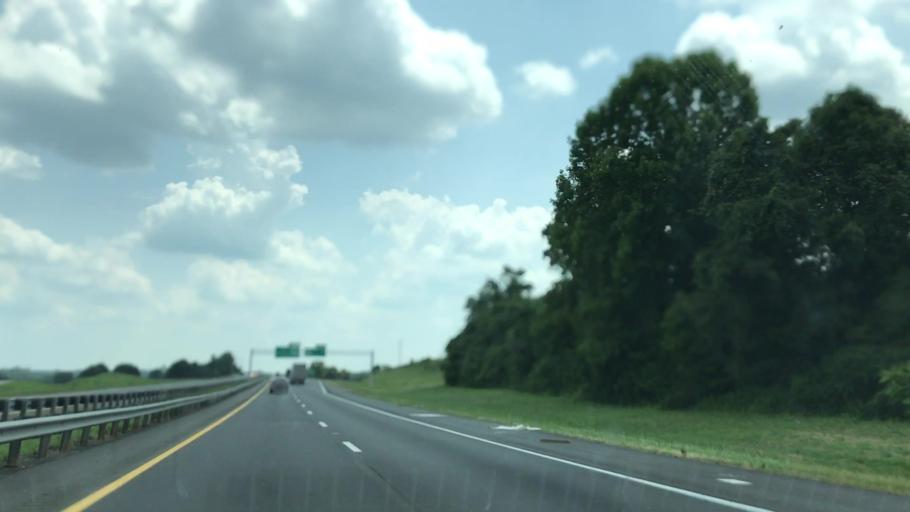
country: US
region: North Carolina
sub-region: Iredell County
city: Statesville
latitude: 35.8170
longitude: -80.8612
